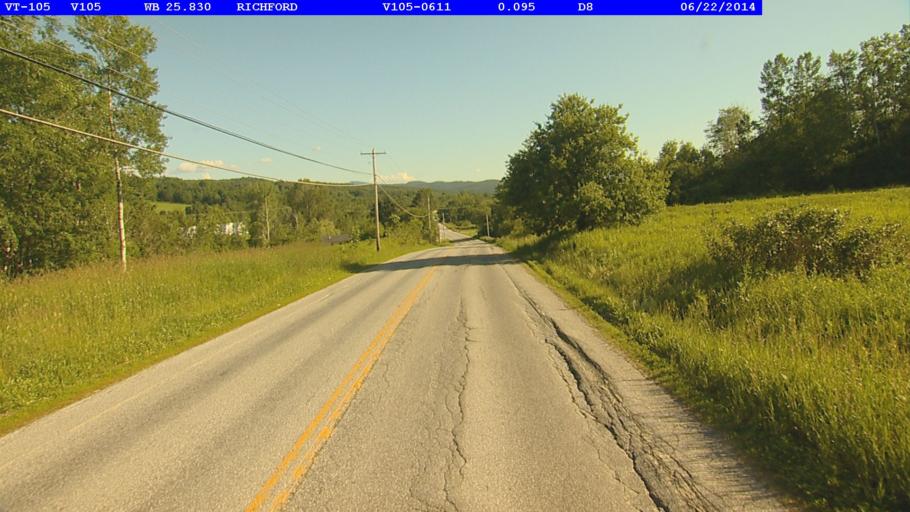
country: US
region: Vermont
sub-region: Franklin County
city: Richford
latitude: 44.9729
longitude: -72.6886
